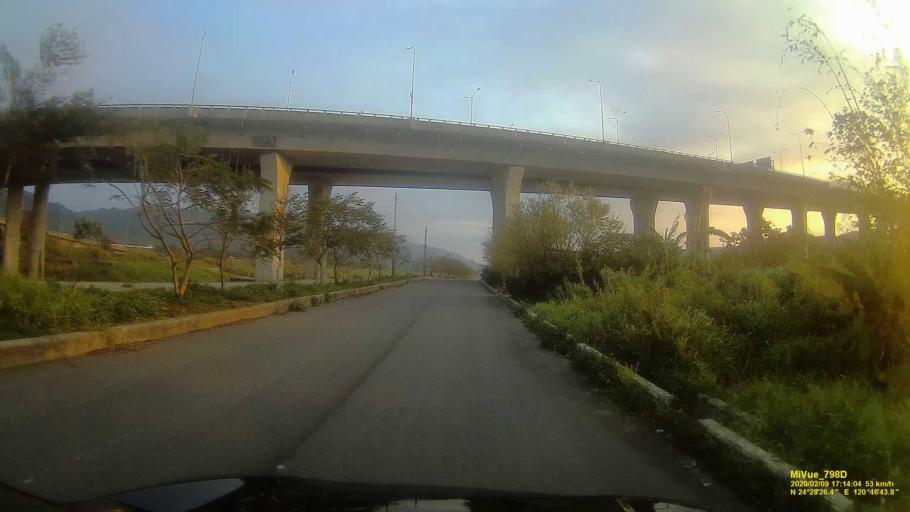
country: TW
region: Taiwan
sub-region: Miaoli
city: Miaoli
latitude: 24.4739
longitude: 120.7788
